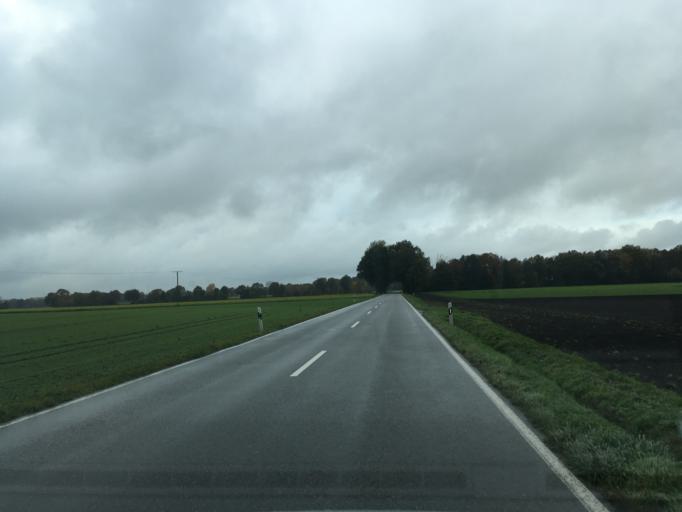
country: DE
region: North Rhine-Westphalia
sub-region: Regierungsbezirk Munster
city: Velen
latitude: 51.8696
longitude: 7.0274
